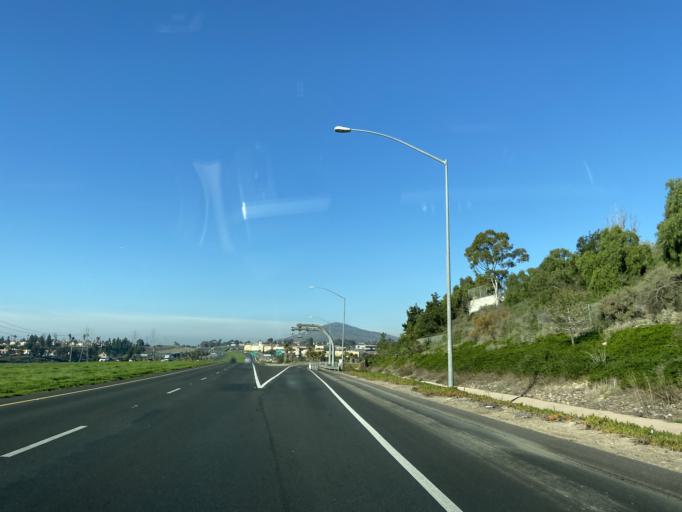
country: US
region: California
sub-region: San Diego County
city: Bonita
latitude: 32.6416
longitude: -116.9705
